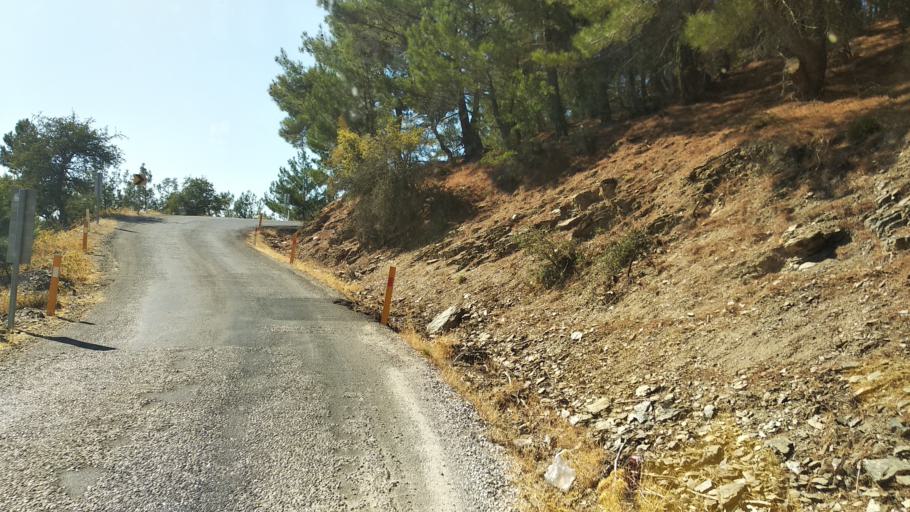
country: TR
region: Izmir
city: Gaziemir
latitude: 38.2968
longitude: 26.9991
